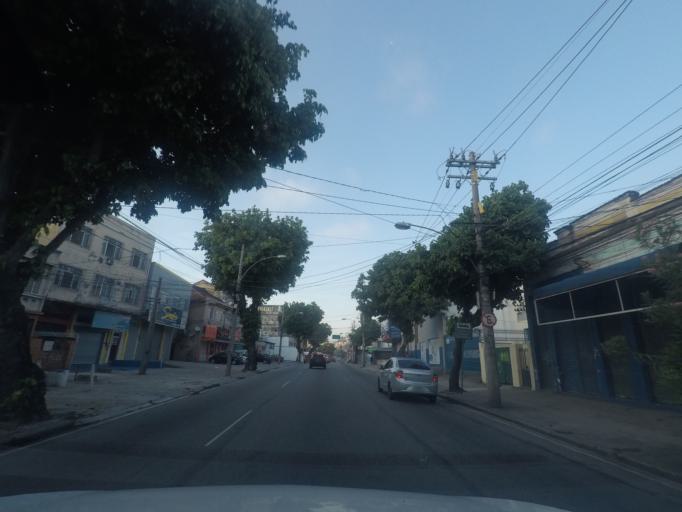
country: BR
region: Rio de Janeiro
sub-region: Duque De Caxias
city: Duque de Caxias
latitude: -22.8314
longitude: -43.2787
